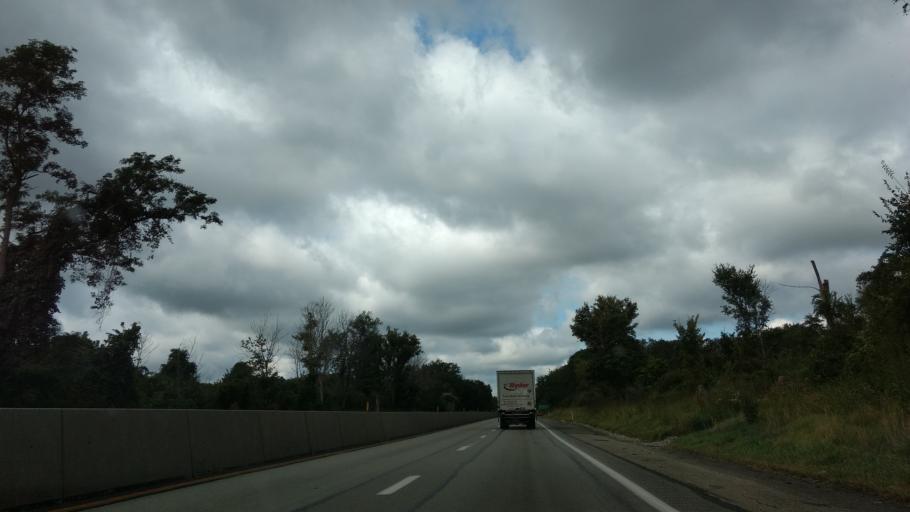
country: US
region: Pennsylvania
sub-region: Westmoreland County
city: Fellsburg
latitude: 40.1530
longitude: -79.7850
